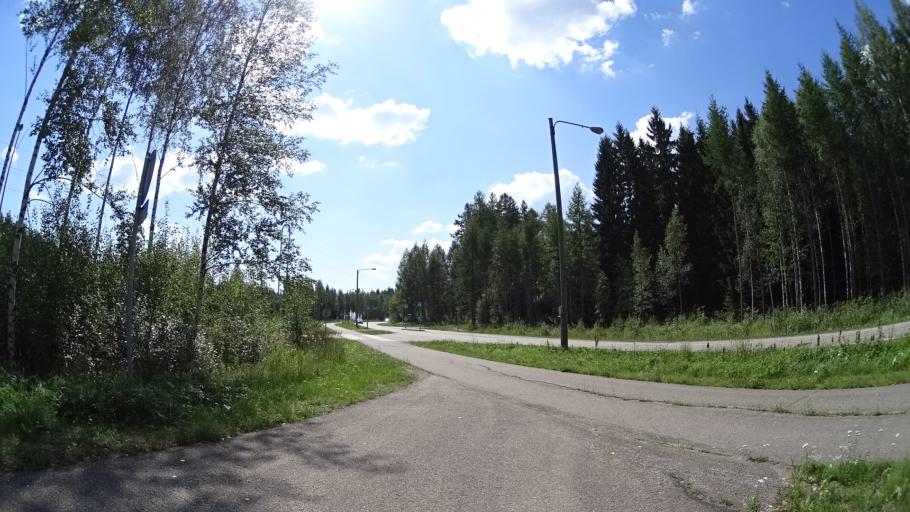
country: FI
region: Uusimaa
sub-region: Helsinki
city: Tuusula
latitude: 60.3574
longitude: 24.9995
